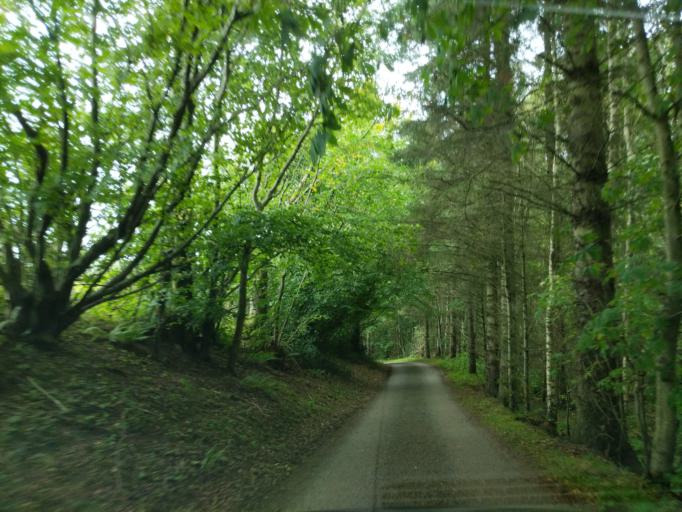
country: GB
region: Scotland
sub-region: The Scottish Borders
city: Galashiels
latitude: 55.5964
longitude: -2.7789
